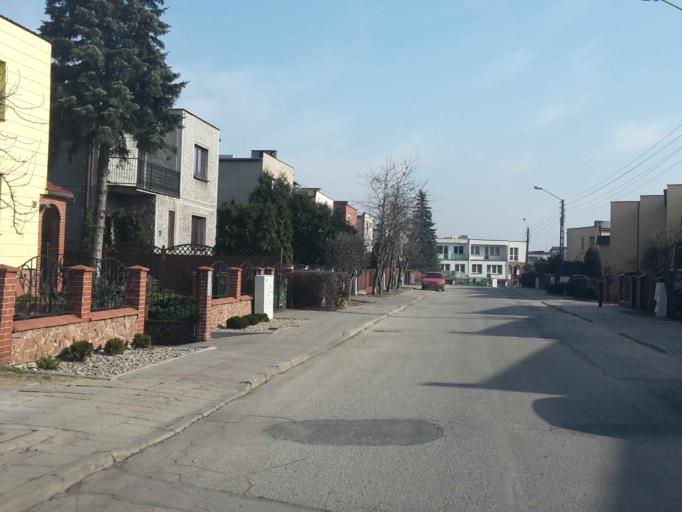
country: PL
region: Kujawsko-Pomorskie
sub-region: Powiat brodnicki
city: Brodnica
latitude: 53.2619
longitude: 19.3814
